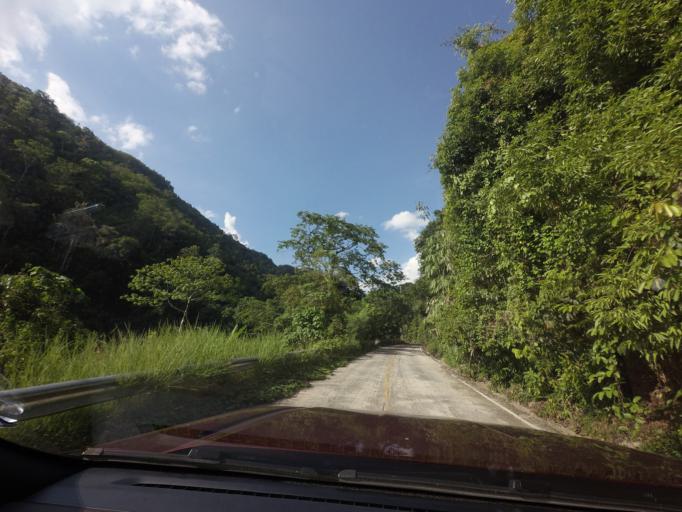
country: TH
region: Yala
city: Than To
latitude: 6.1344
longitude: 101.3001
